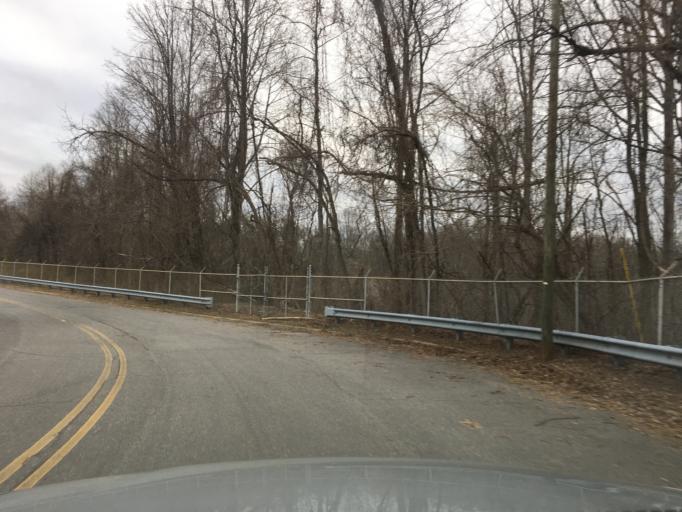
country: US
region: North Carolina
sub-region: Buncombe County
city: Woodfin
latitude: 35.6077
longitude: -82.5831
